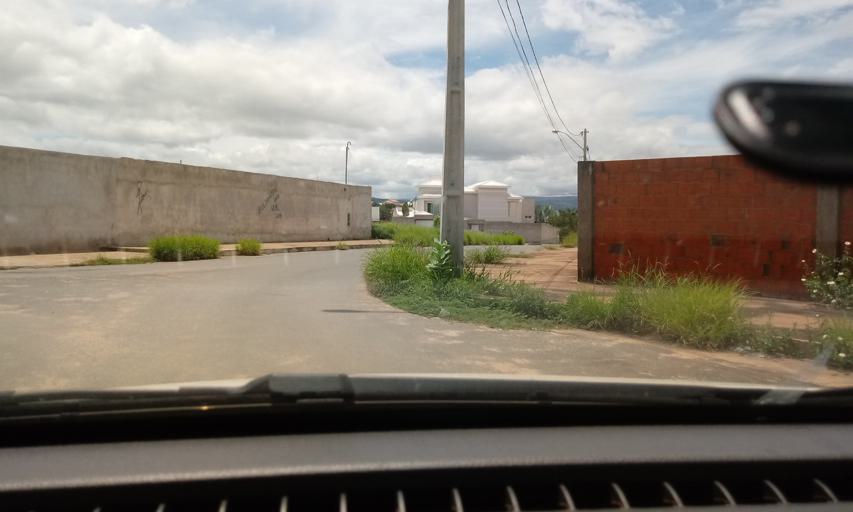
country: BR
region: Bahia
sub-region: Guanambi
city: Guanambi
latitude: -14.2292
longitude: -42.7750
